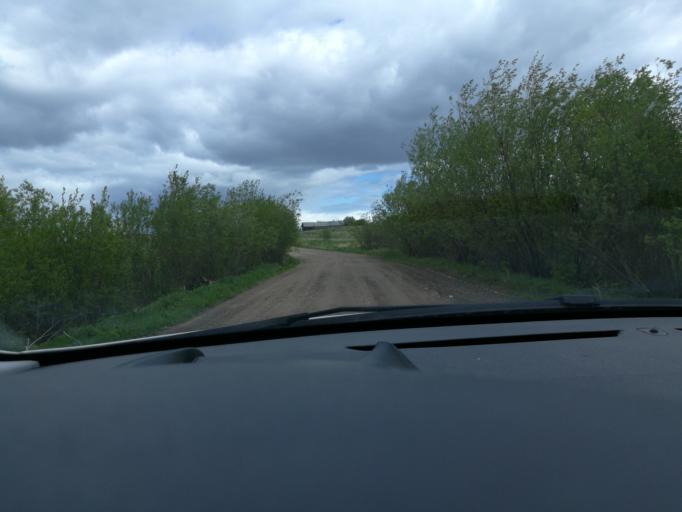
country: RU
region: Arkhangelskaya
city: Lukovetskiy
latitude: 64.2556
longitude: 41.7977
